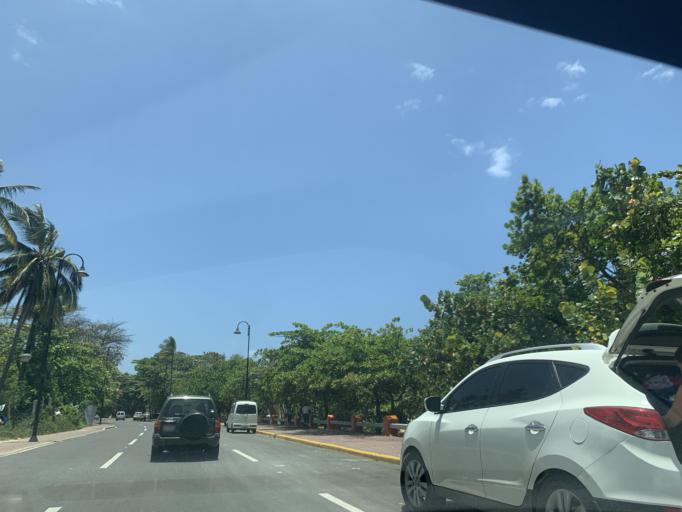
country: DO
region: Puerto Plata
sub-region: Puerto Plata
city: Puerto Plata
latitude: 19.7863
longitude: -70.6676
